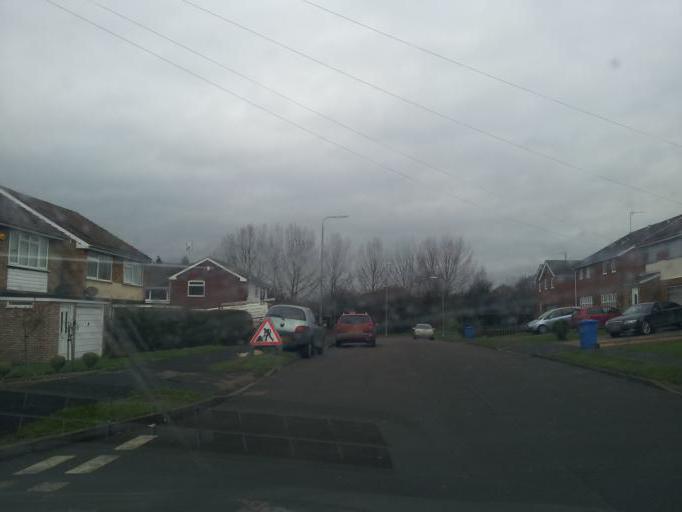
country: GB
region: England
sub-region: Northamptonshire
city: Kettering
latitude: 52.3963
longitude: -0.7012
